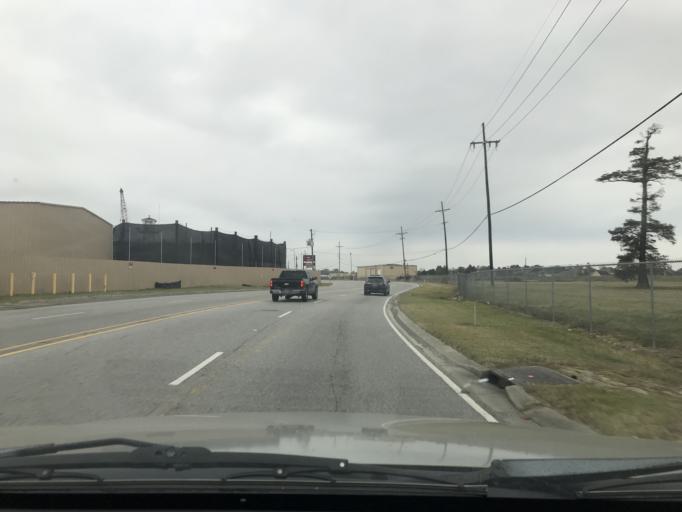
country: US
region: Louisiana
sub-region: Jefferson Parish
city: Harvey
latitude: 29.8827
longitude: -90.0758
